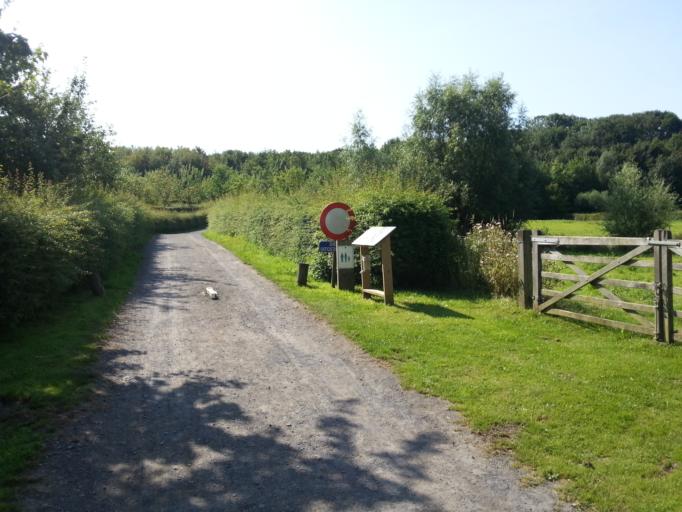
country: BE
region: Flanders
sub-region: Provincie West-Vlaanderen
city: Ieper
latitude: 50.8179
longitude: 2.9097
